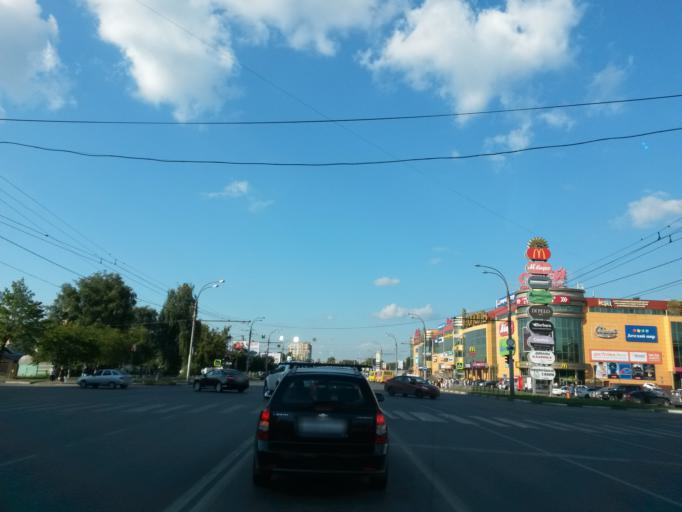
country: RU
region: Ivanovo
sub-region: Gorod Ivanovo
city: Ivanovo
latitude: 56.9810
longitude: 40.9794
